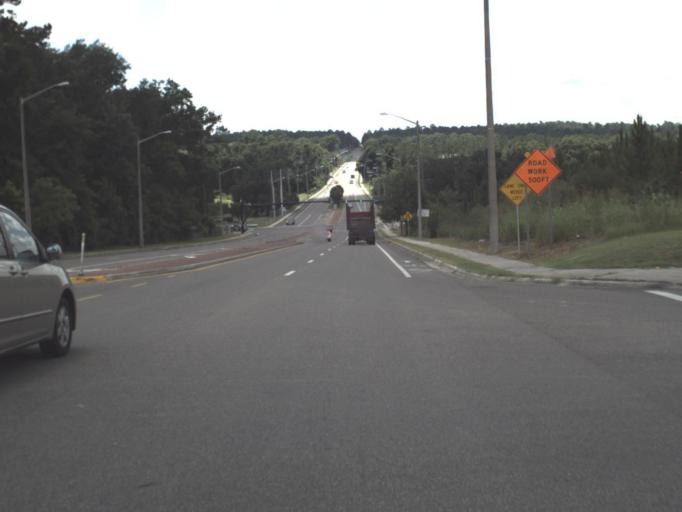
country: US
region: Florida
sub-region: Alachua County
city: Alachua
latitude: 29.6891
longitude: -82.4503
